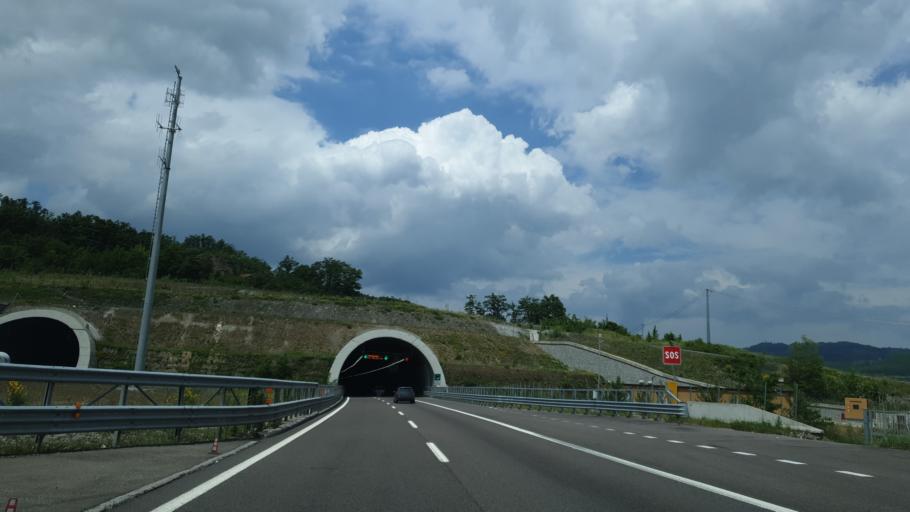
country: IT
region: Emilia-Romagna
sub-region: Provincia di Bologna
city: Castiglione dei Pepoli
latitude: 44.1655
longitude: 11.1970
